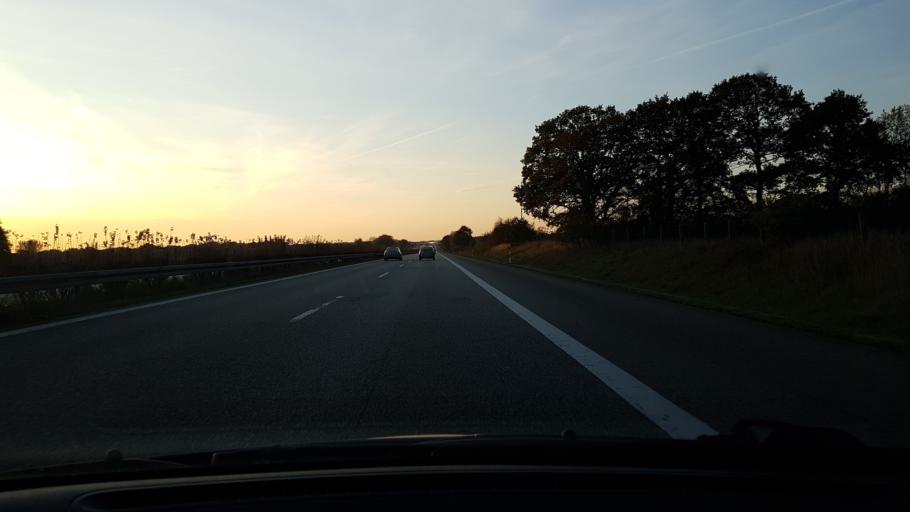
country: DE
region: Mecklenburg-Vorpommern
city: Wittenburg
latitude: 53.5006
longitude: 11.0574
